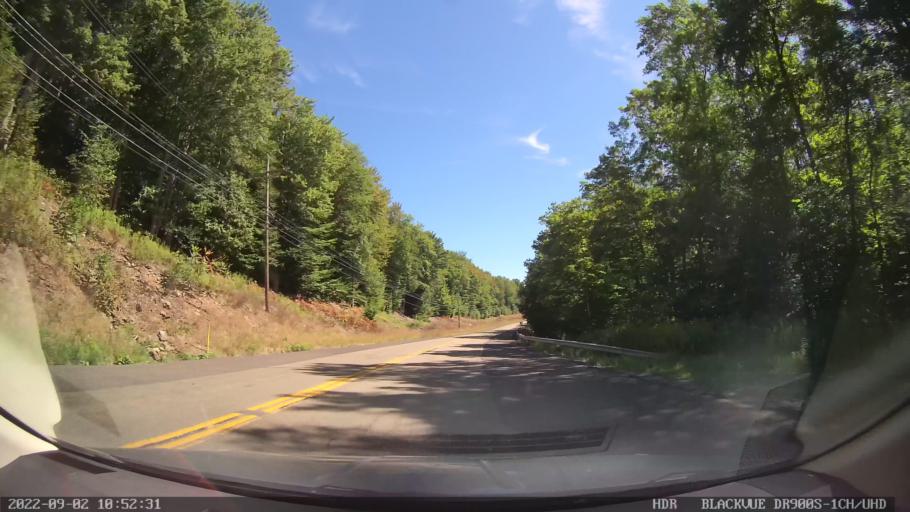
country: US
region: Pennsylvania
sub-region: Tioga County
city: Blossburg
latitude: 41.6387
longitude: -77.1086
